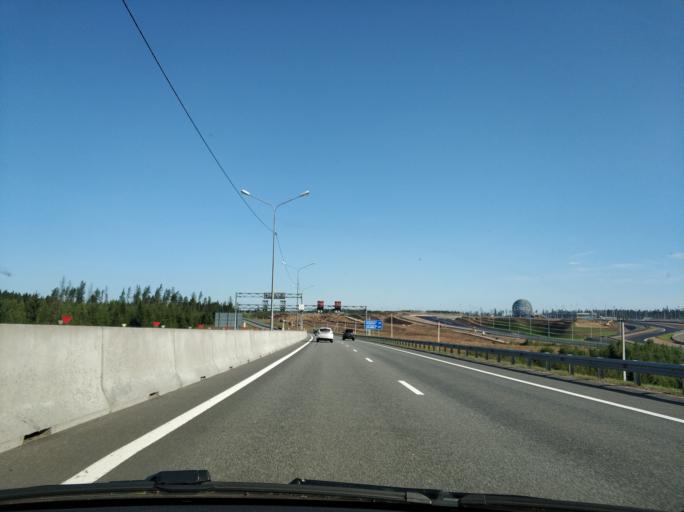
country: RU
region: Leningrad
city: Sosnovo
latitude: 60.5036
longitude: 30.1943
